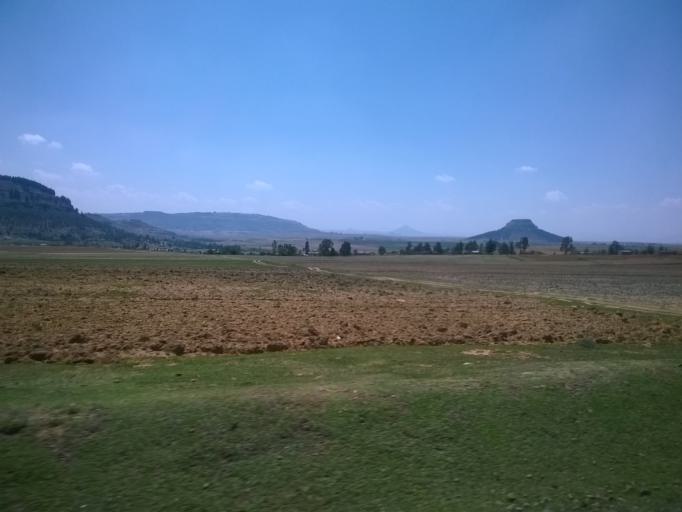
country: LS
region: Leribe
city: Maputsoe
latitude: -28.9682
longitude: 27.9664
